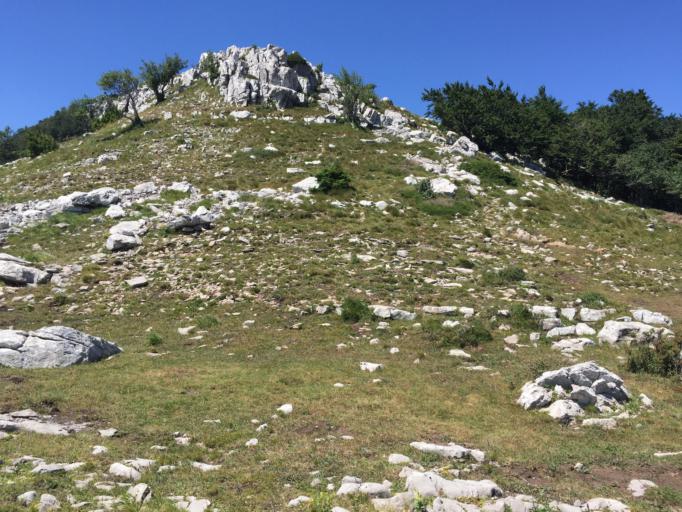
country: HR
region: Primorsko-Goranska
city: Drazice
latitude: 45.4471
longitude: 14.4727
